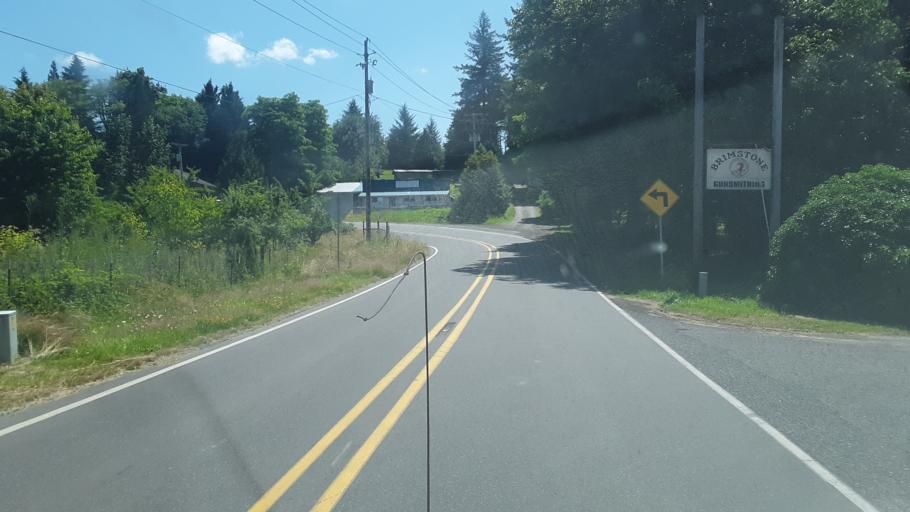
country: US
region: Washington
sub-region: Clark County
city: Amboy
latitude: 45.9095
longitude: -122.4521
